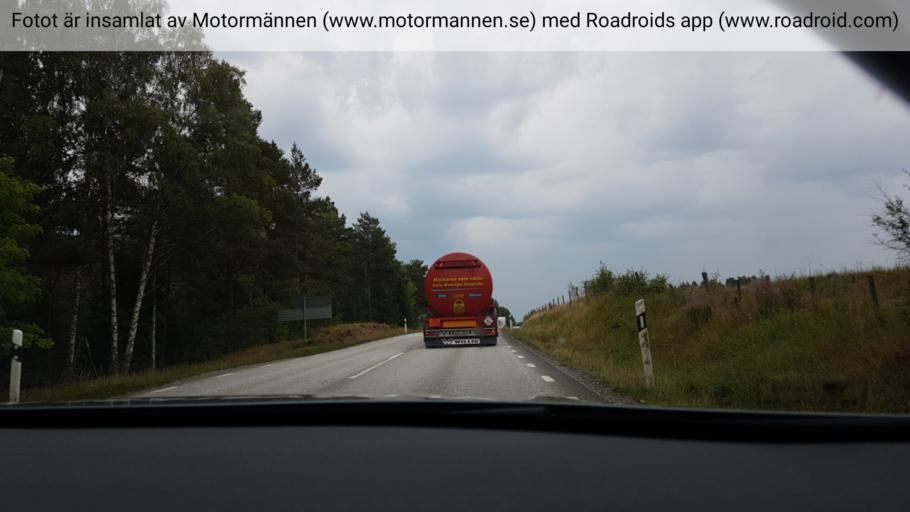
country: SE
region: Joenkoeping
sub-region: Mullsjo Kommun
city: Mullsjoe
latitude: 57.8711
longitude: 13.9522
